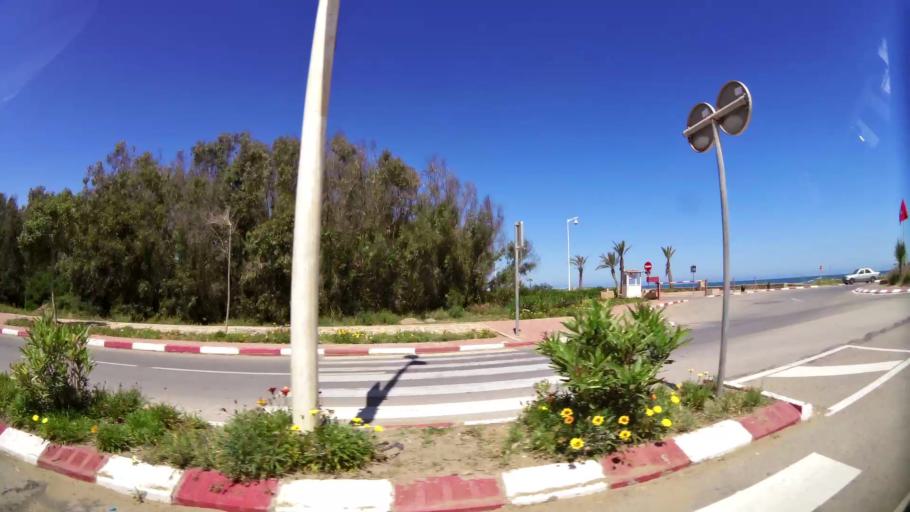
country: MA
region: Oriental
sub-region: Berkane-Taourirt
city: Madagh
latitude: 35.0971
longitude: -2.2646
